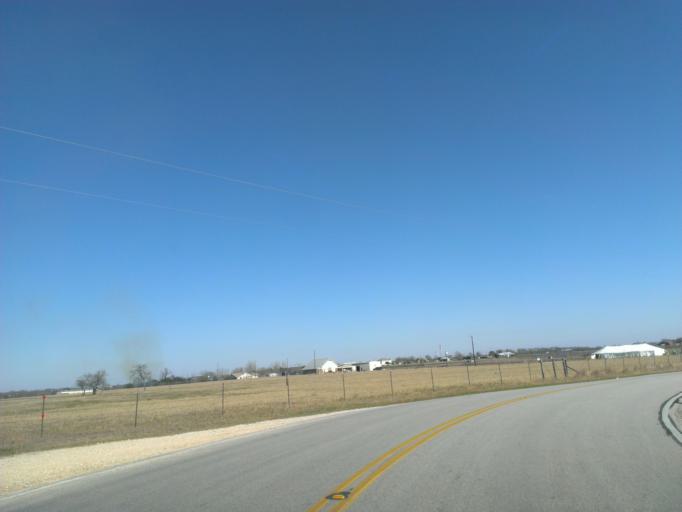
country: US
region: Texas
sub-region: Williamson County
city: Georgetown
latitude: 30.6626
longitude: -97.5825
